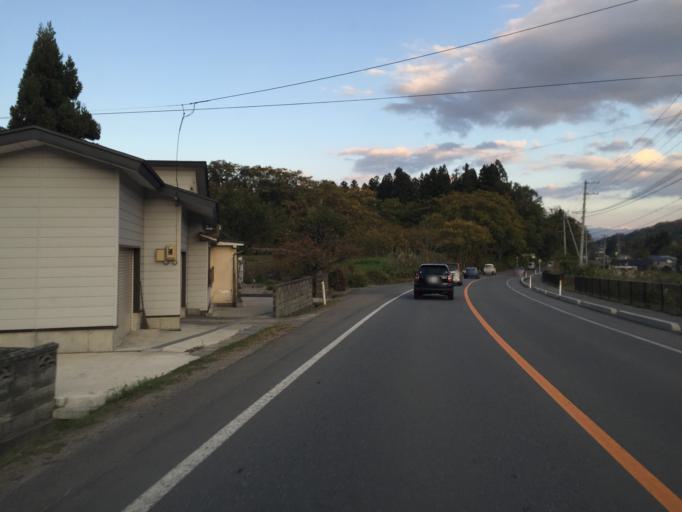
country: JP
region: Yamagata
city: Yonezawa
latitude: 37.9150
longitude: 140.0616
